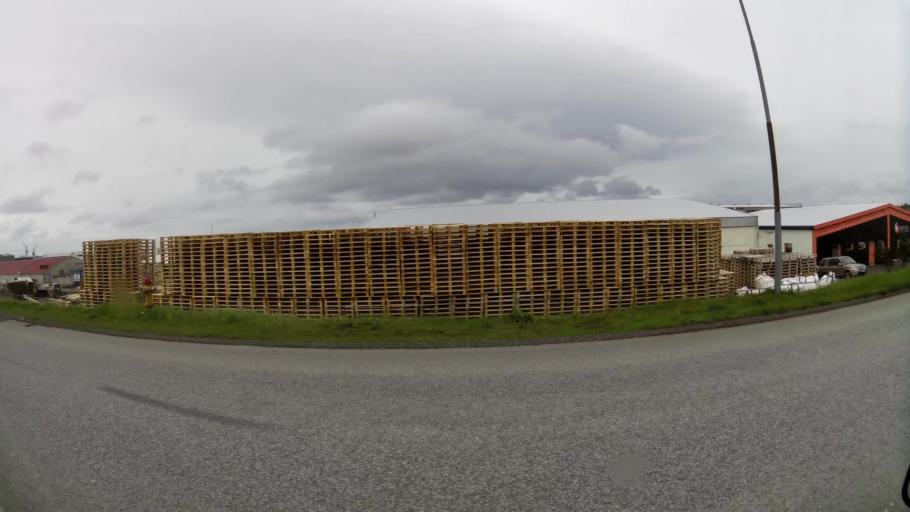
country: IS
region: Capital Region
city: Hafnarfjoerdur
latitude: 64.0624
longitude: -21.9676
